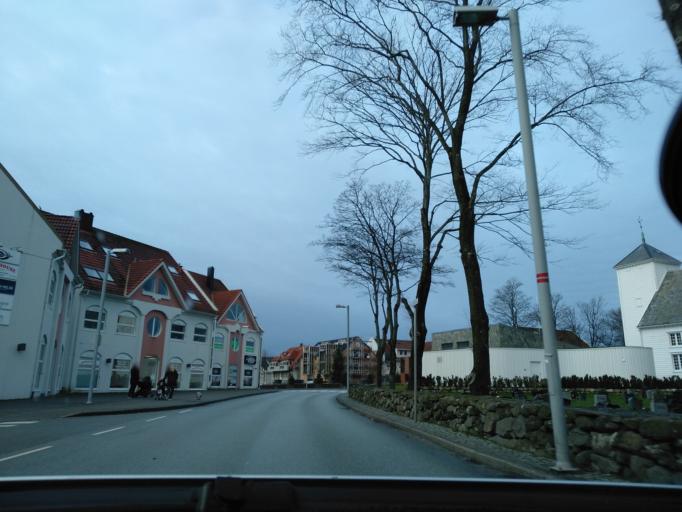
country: NO
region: Rogaland
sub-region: Randaberg
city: Randaberg
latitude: 58.9993
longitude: 5.6199
